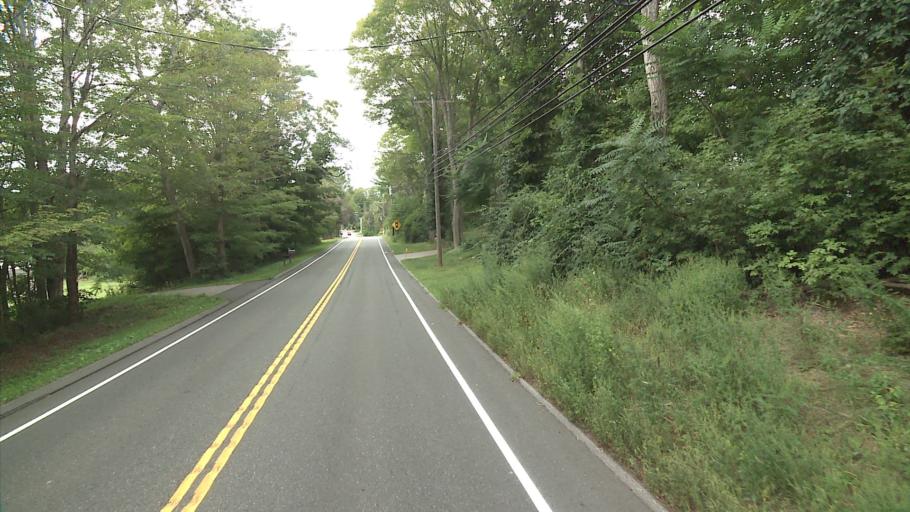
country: US
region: Connecticut
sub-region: New London County
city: Colchester
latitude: 41.4977
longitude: -72.2812
